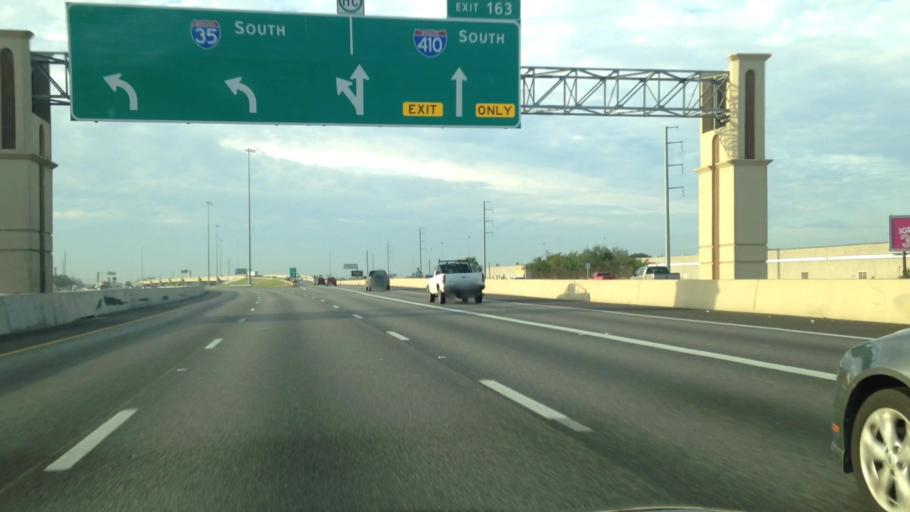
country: US
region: Texas
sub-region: Bexar County
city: Kirby
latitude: 29.4809
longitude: -98.4022
